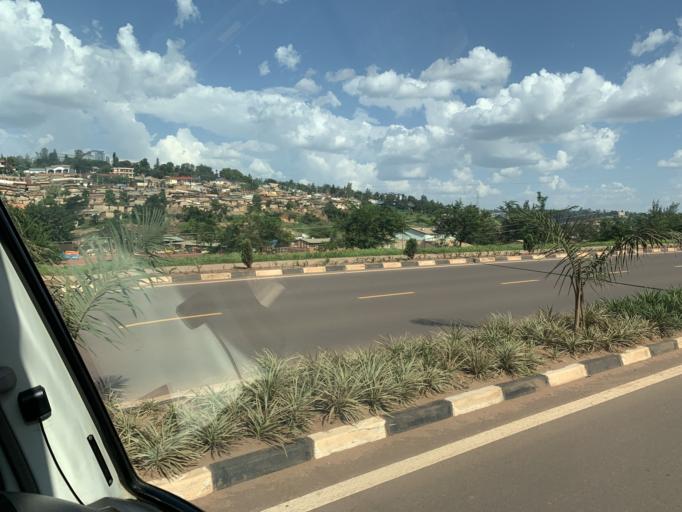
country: RW
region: Kigali
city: Kigali
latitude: -1.9582
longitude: 30.0765
